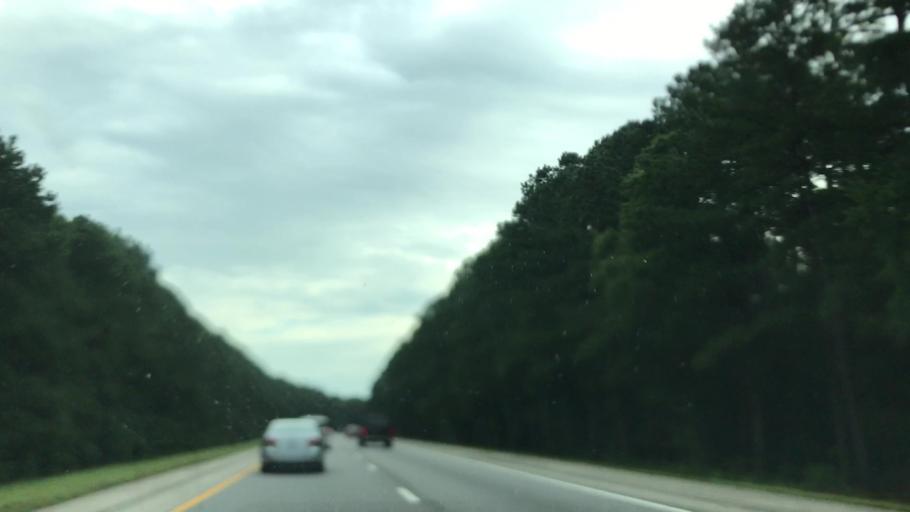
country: US
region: North Carolina
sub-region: Wilson County
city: Lucama
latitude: 35.7128
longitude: -78.0388
